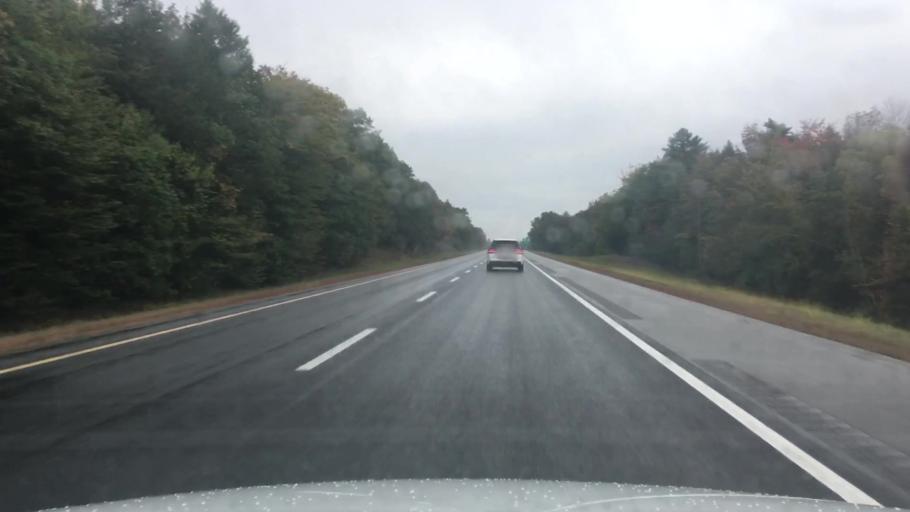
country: US
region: Maine
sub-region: Sagadahoc County
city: Topsham
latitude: 43.9969
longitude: -69.9321
